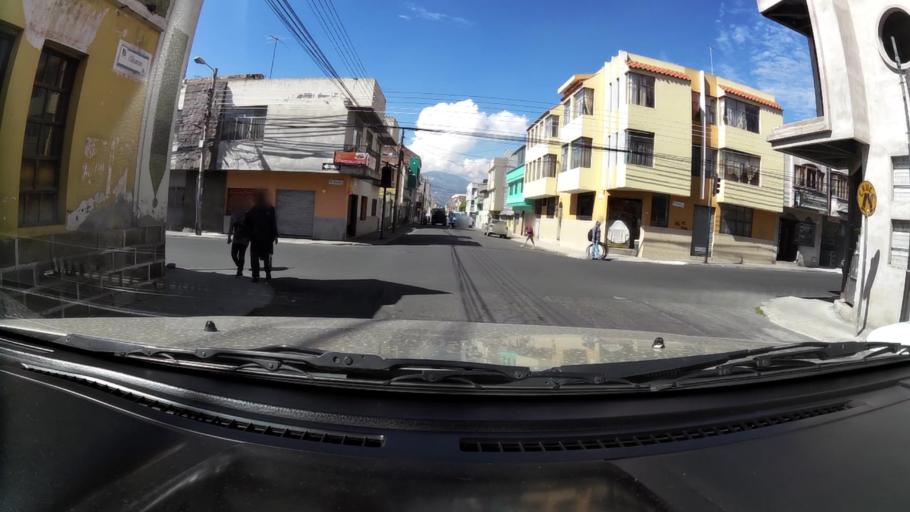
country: EC
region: Chimborazo
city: Riobamba
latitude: -1.6664
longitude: -78.6503
